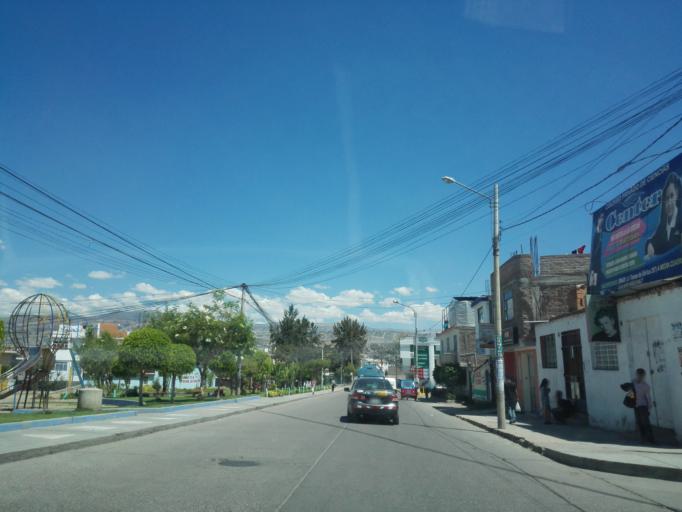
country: PE
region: Ayacucho
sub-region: Provincia de Huamanga
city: Ayacucho
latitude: -13.1510
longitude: -74.2276
